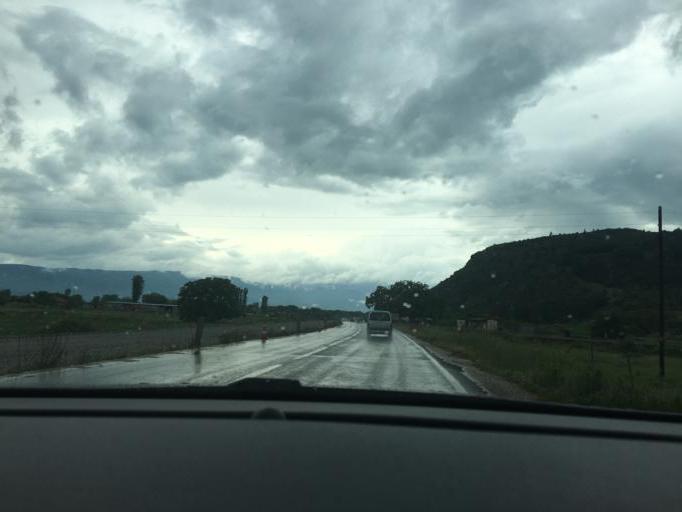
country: MK
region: Ohrid
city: Ohrid
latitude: 41.1364
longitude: 20.7714
